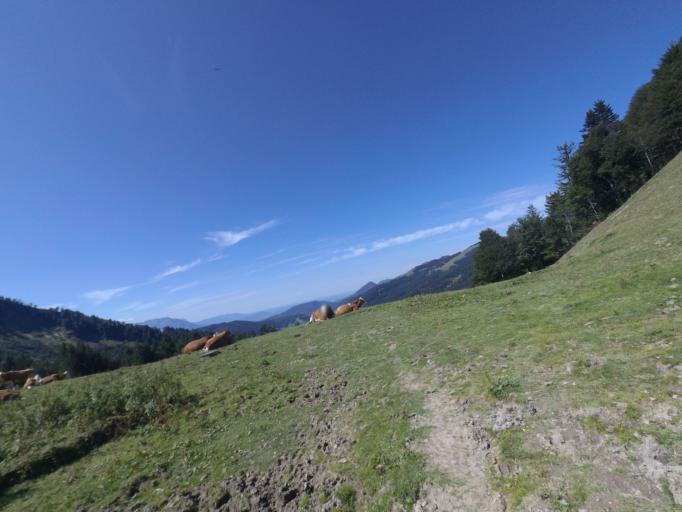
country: AT
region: Salzburg
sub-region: Politischer Bezirk Salzburg-Umgebung
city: Hintersee
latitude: 47.6889
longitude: 13.2525
